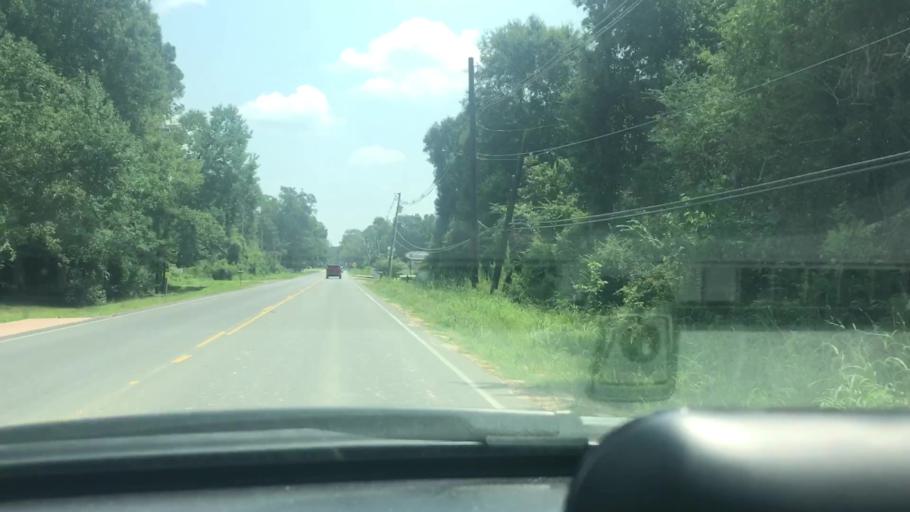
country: US
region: Louisiana
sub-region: Livingston Parish
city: Denham Springs
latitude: 30.4835
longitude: -90.9314
